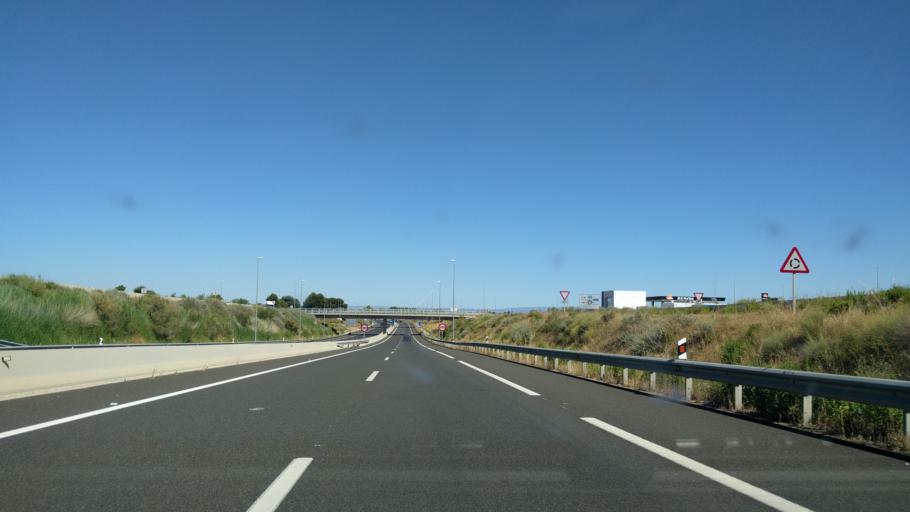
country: ES
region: Catalonia
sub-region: Provincia de Lleida
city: Alpicat
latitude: 41.6495
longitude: 0.5572
